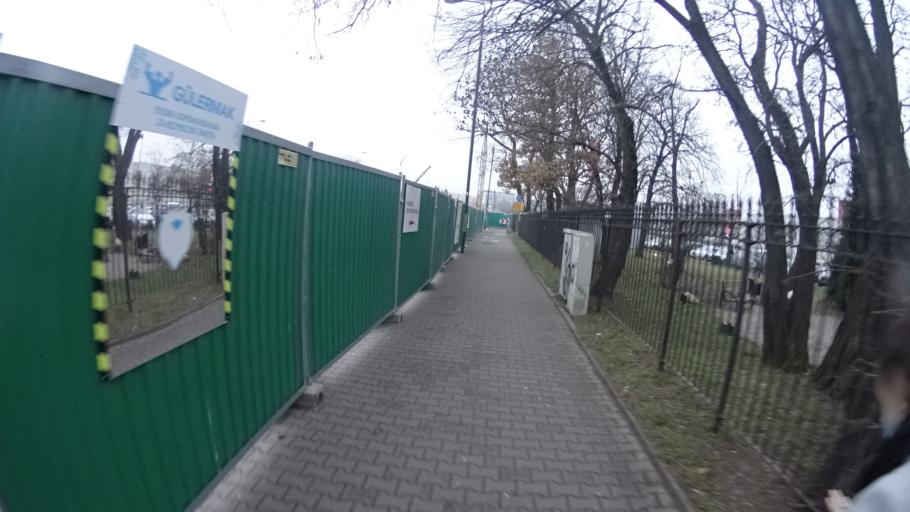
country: PL
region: Masovian Voivodeship
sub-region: Warszawa
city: Bemowo
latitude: 52.2406
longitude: 20.9316
